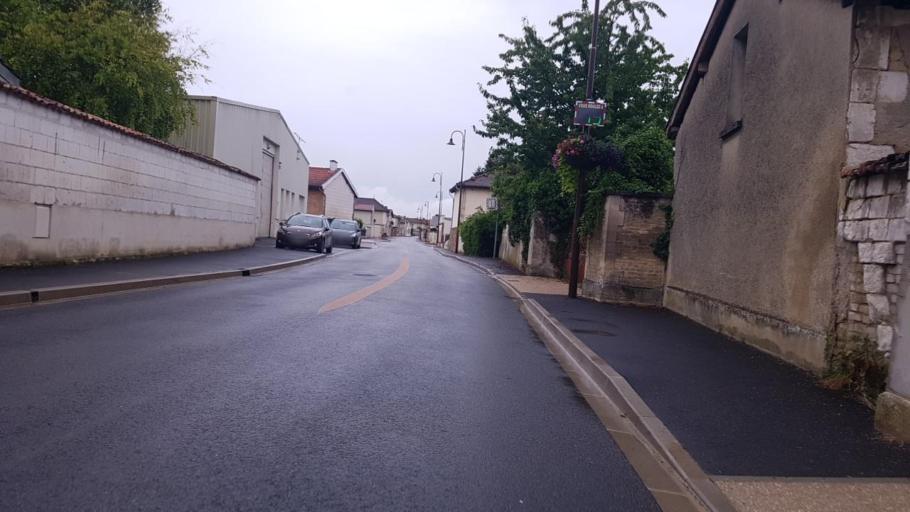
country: FR
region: Champagne-Ardenne
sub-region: Departement de la Marne
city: Sarry
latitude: 48.9170
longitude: 4.4099
